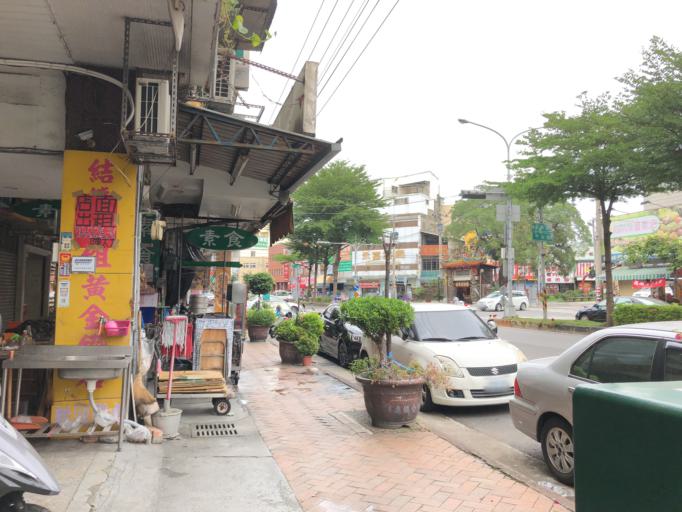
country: TW
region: Taiwan
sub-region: Taichung City
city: Taichung
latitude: 24.2376
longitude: 120.5598
